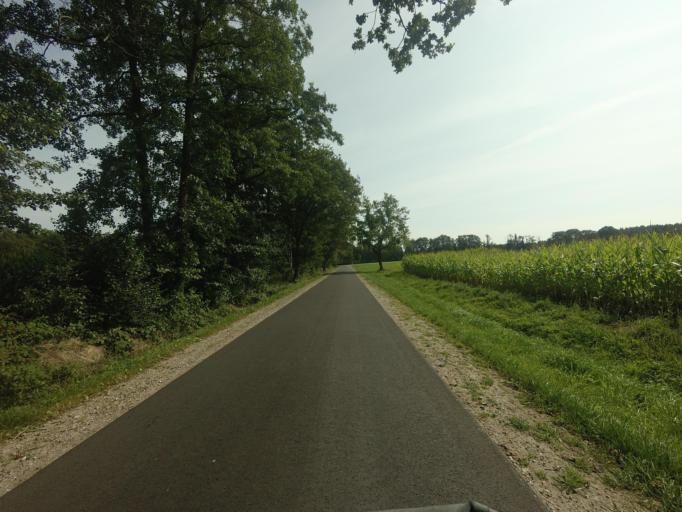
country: DE
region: Lower Saxony
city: Itterbeck
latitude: 52.5288
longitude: 6.7651
